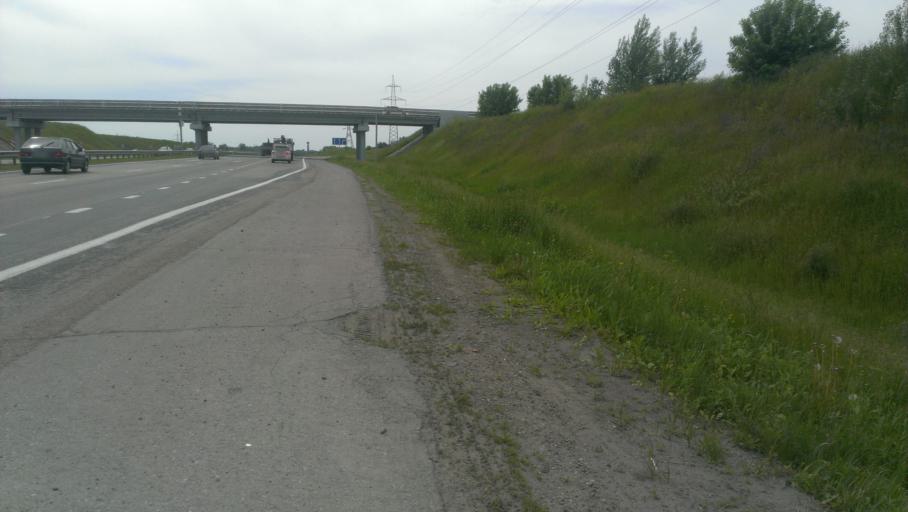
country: RU
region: Altai Krai
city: Sannikovo
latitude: 53.3416
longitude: 83.9374
